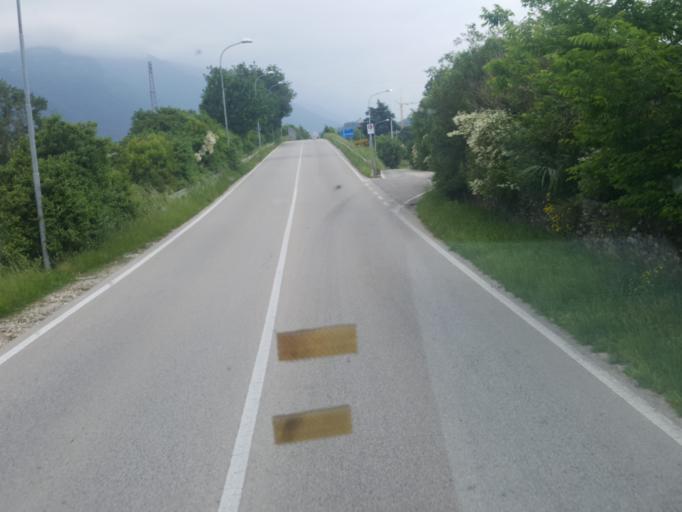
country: IT
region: Veneto
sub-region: Provincia di Vicenza
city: Romano d'Ezzelino
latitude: 45.7847
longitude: 11.7519
